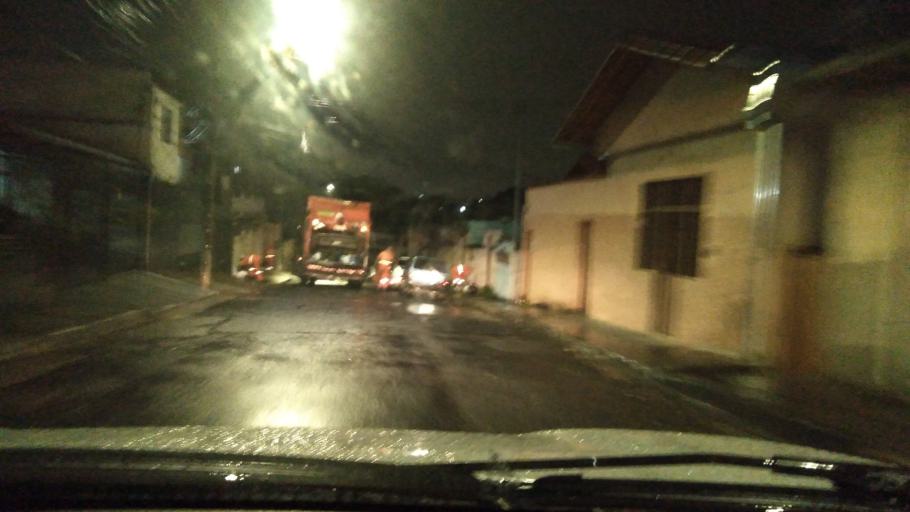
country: BR
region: Minas Gerais
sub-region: Belo Horizonte
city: Belo Horizonte
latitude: -19.8985
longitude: -43.9583
